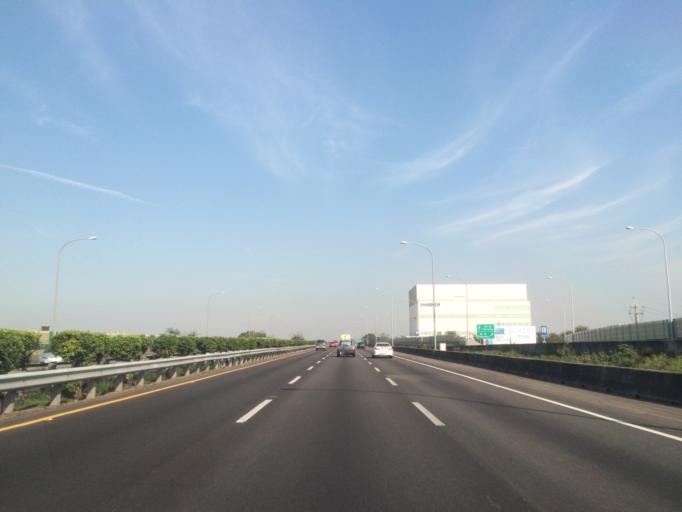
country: TW
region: Taiwan
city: Fengyuan
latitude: 24.2460
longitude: 120.6899
